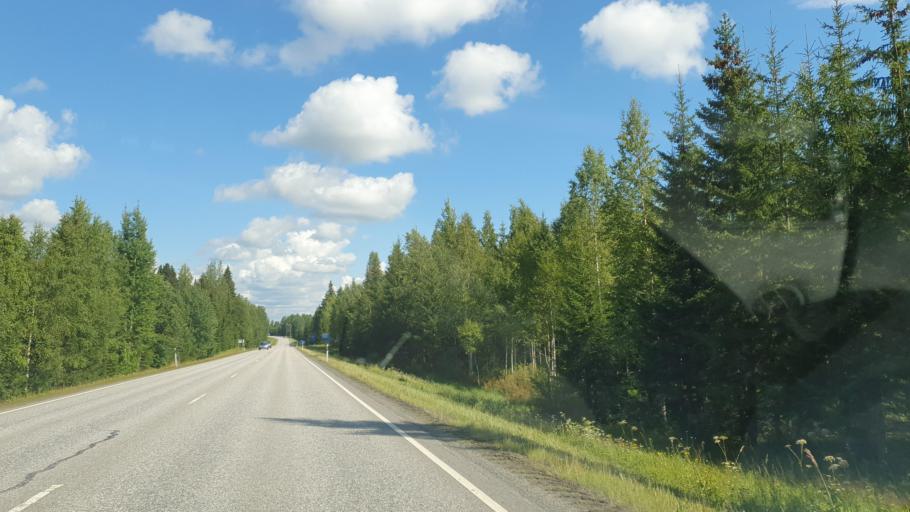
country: FI
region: Northern Savo
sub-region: Ylae-Savo
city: Sonkajaervi
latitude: 63.6908
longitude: 27.3477
